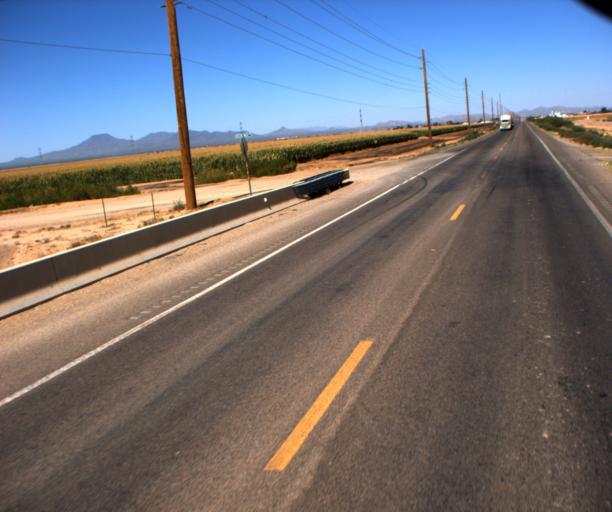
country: US
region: Arizona
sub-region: Pinal County
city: Casa Grande
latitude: 32.8794
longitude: -111.9334
